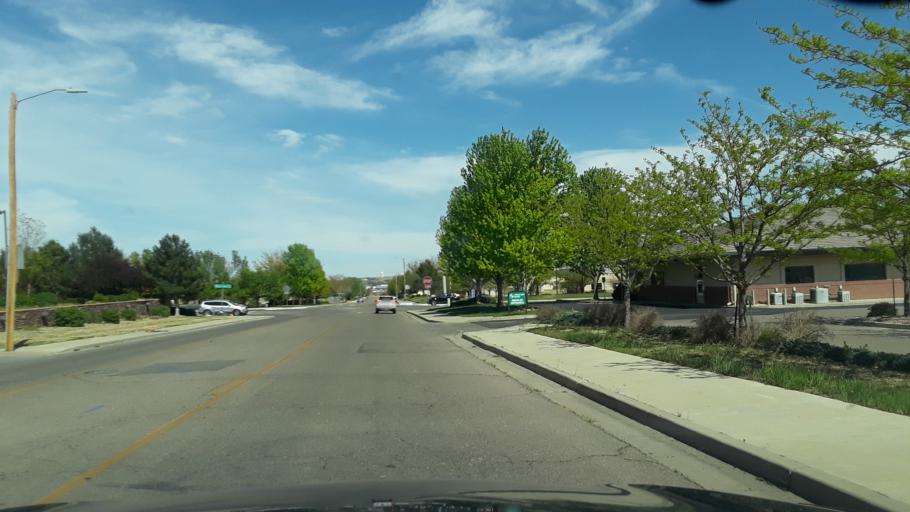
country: US
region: Colorado
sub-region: Pueblo County
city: Pueblo
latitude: 38.3124
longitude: -104.6280
